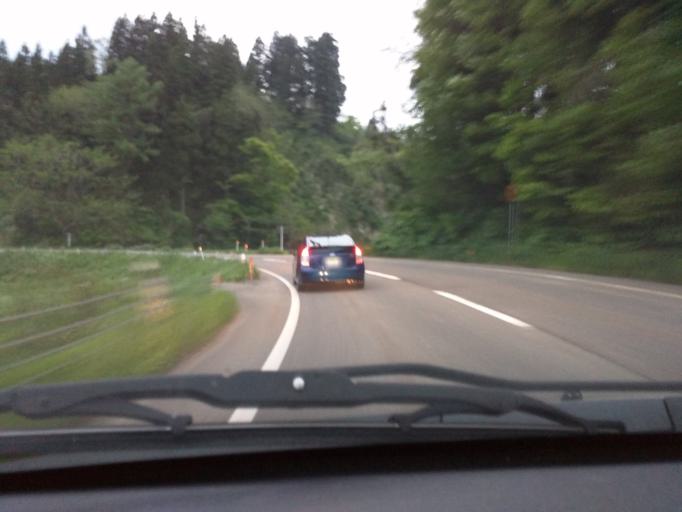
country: JP
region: Niigata
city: Ojiya
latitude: 37.3232
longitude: 138.6842
